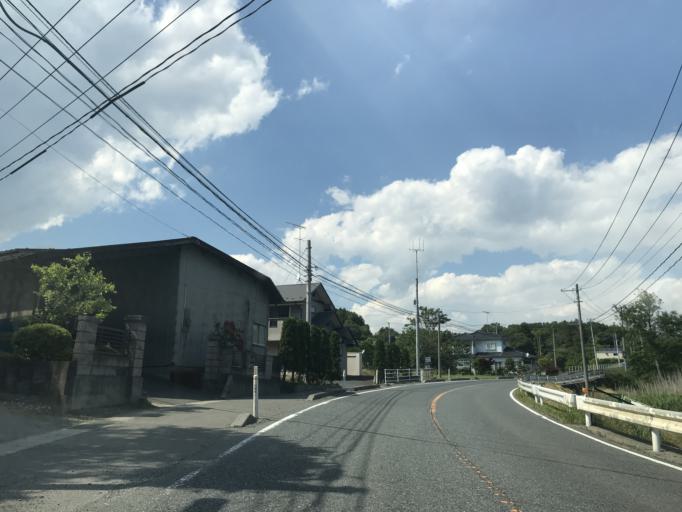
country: JP
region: Miyagi
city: Wakuya
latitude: 38.4882
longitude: 141.1076
